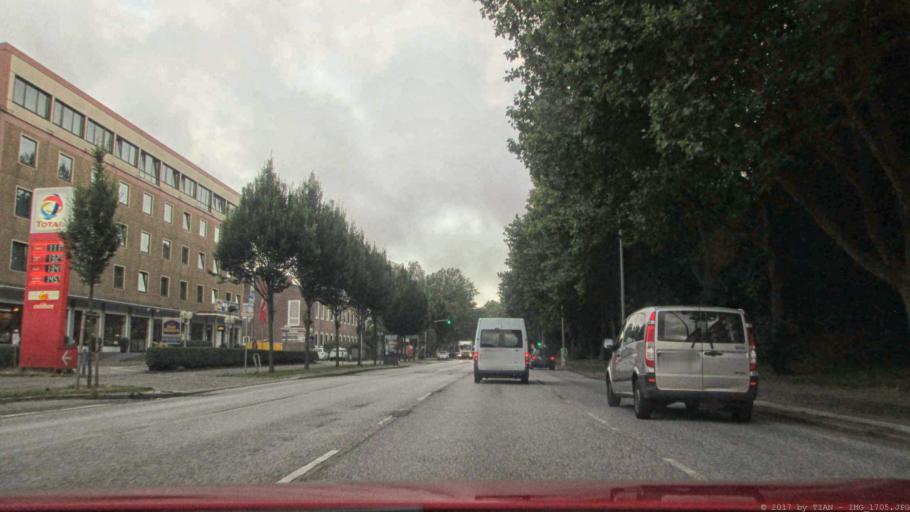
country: DE
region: Hamburg
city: Marienthal
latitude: 53.5543
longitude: 10.0634
